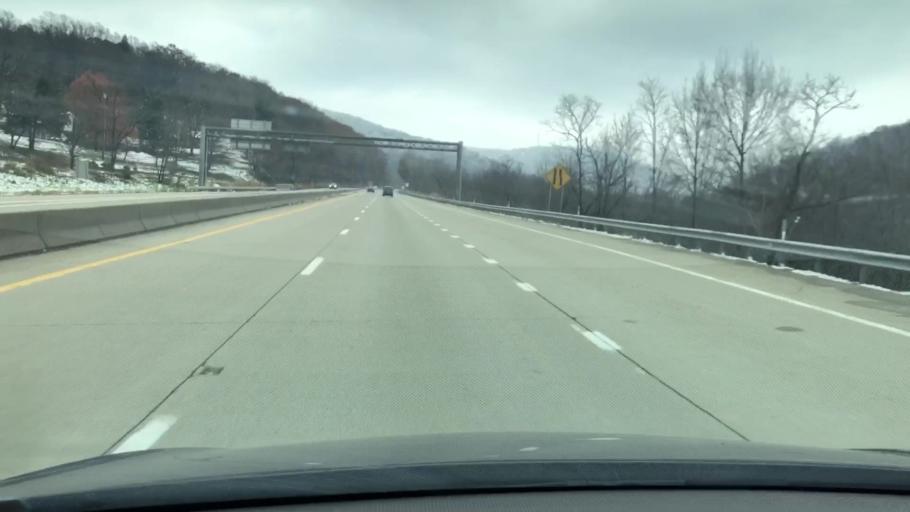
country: US
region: Pennsylvania
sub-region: Fayette County
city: Hopwood
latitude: 39.8678
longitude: -79.6921
